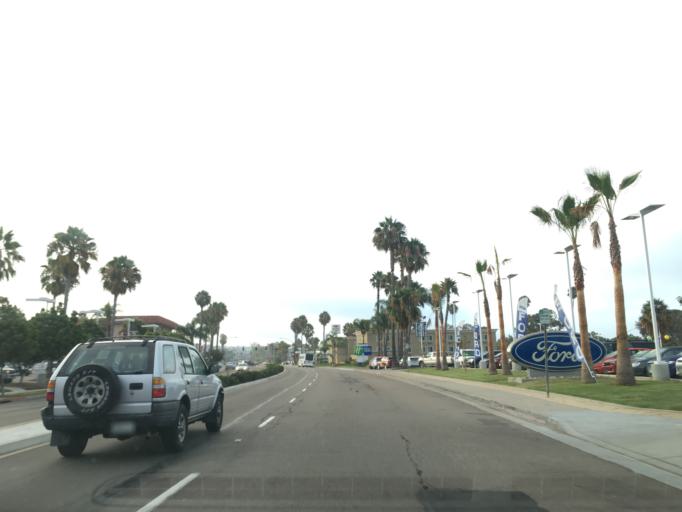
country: US
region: California
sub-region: San Diego County
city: La Jolla
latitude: 32.8044
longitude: -117.2181
